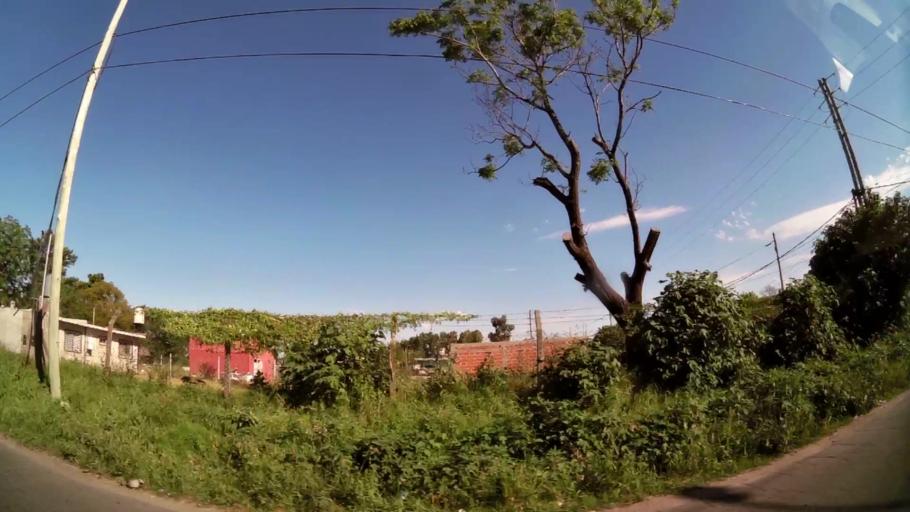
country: AR
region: Buenos Aires
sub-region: Partido de Tigre
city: Tigre
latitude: -34.4861
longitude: -58.6561
